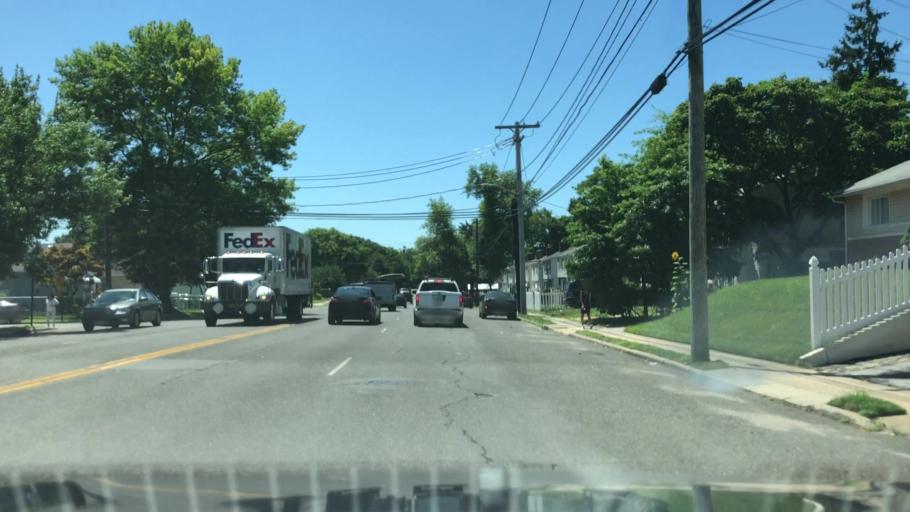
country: US
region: New York
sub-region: Nassau County
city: Hempstead
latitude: 40.7009
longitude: -73.6313
